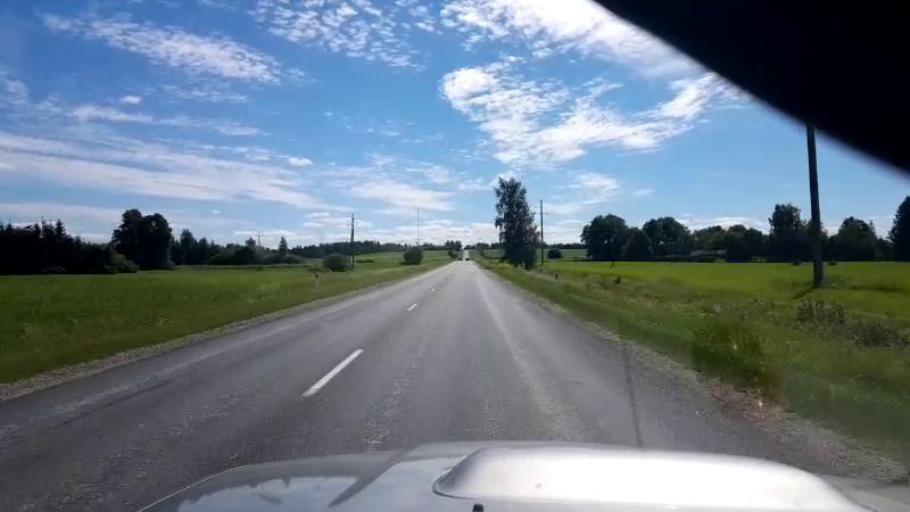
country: EE
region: Laeaene-Virumaa
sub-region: Rakke vald
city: Rakke
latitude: 58.8607
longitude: 26.2933
